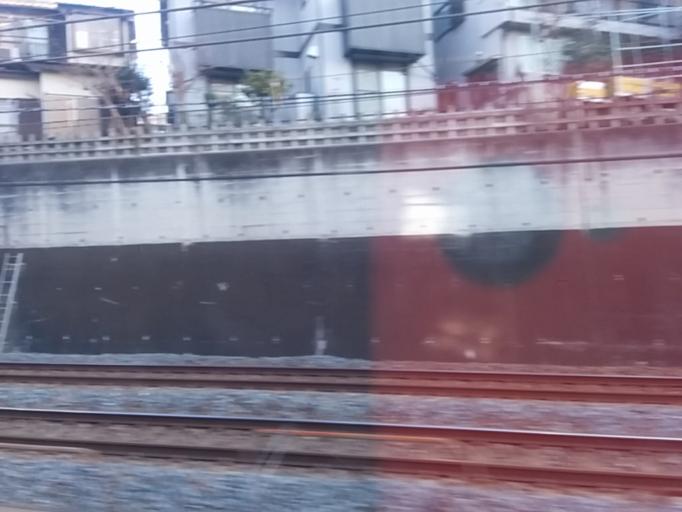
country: JP
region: Saitama
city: Asaka
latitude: 35.8079
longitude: 139.5959
